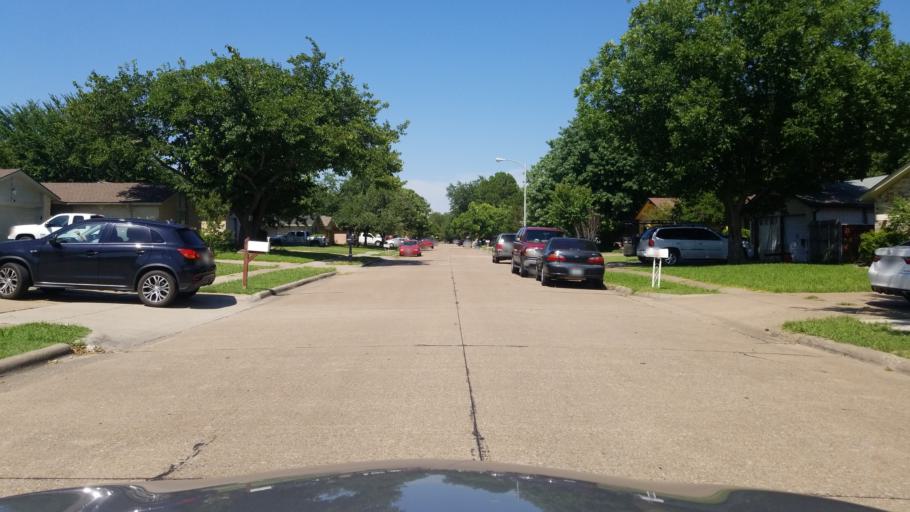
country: US
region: Texas
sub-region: Dallas County
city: Grand Prairie
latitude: 32.6877
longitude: -97.0123
